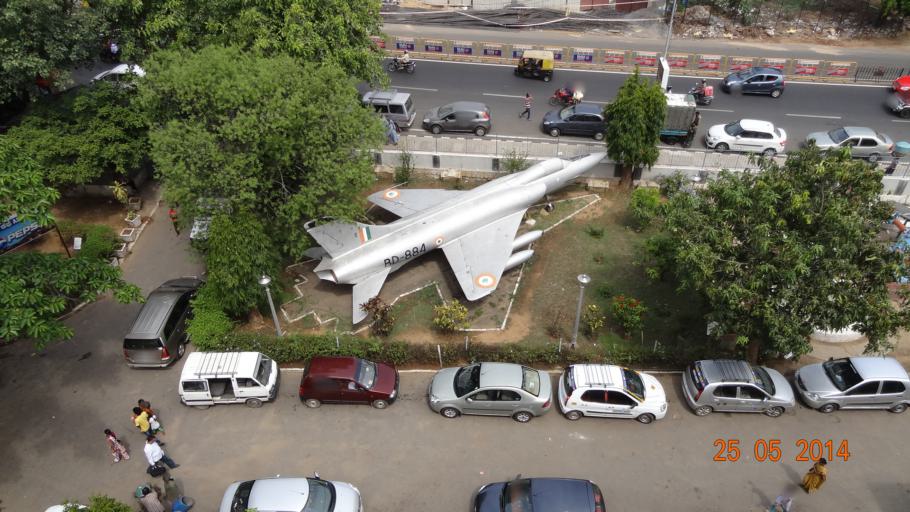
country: IN
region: Karnataka
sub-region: Bangalore Urban
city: Bangalore
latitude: 12.9752
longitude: 77.5966
